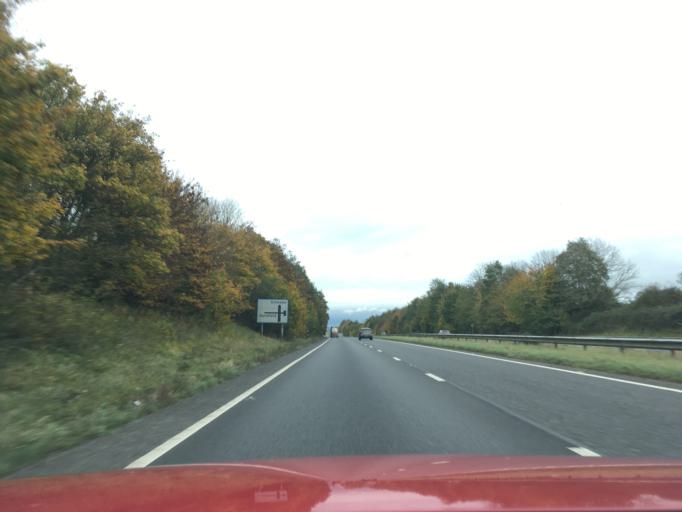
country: GB
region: England
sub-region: Somerset
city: Stoke-sub-Hamdon
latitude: 50.9770
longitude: -2.7251
